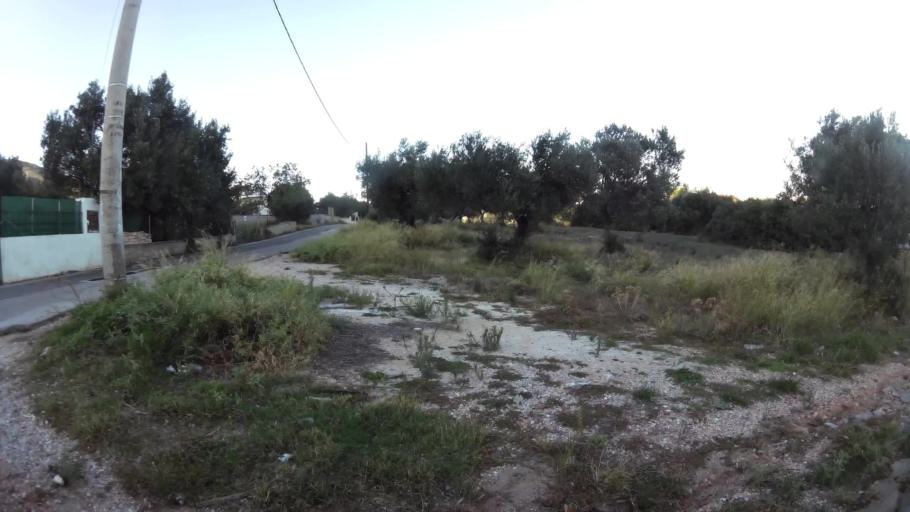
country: GR
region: Attica
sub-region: Nomarchia Anatolikis Attikis
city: Paiania
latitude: 37.9670
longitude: 23.8444
